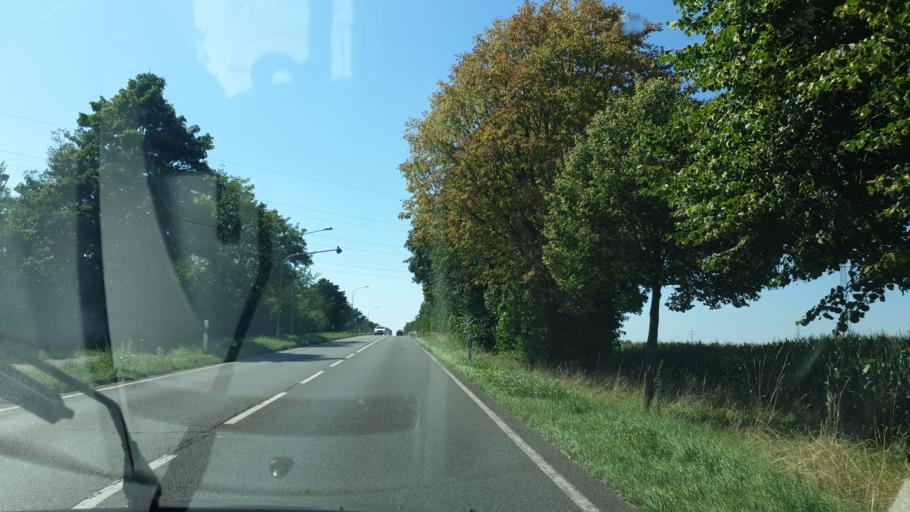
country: DE
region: North Rhine-Westphalia
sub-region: Regierungsbezirk Koln
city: Euskirchen
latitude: 50.6565
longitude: 6.7667
